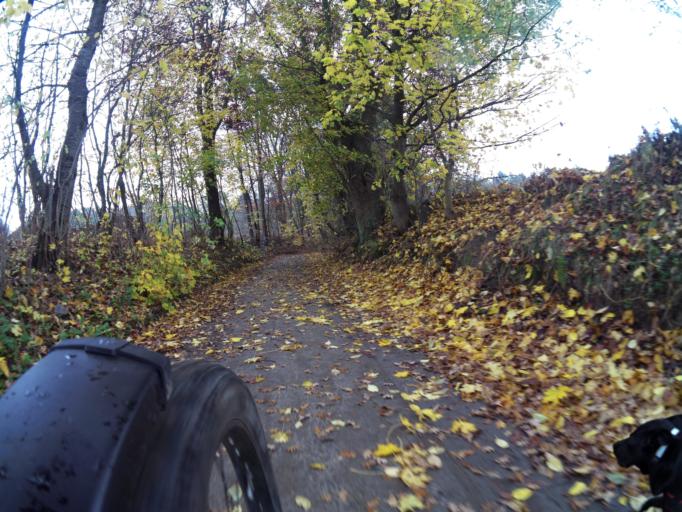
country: PL
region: Pomeranian Voivodeship
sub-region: Powiat pucki
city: Krokowa
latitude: 54.7831
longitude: 18.0878
